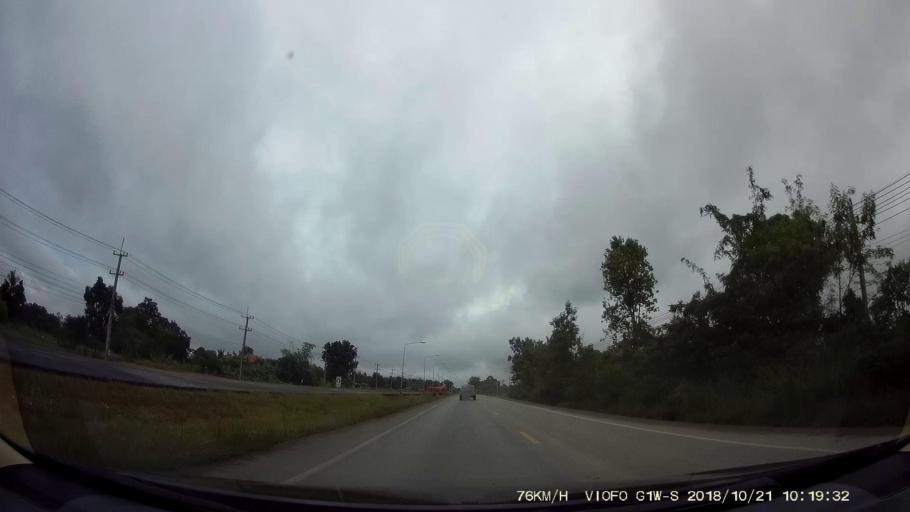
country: TH
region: Chaiyaphum
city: Phu Khiao
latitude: 16.3136
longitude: 102.1993
